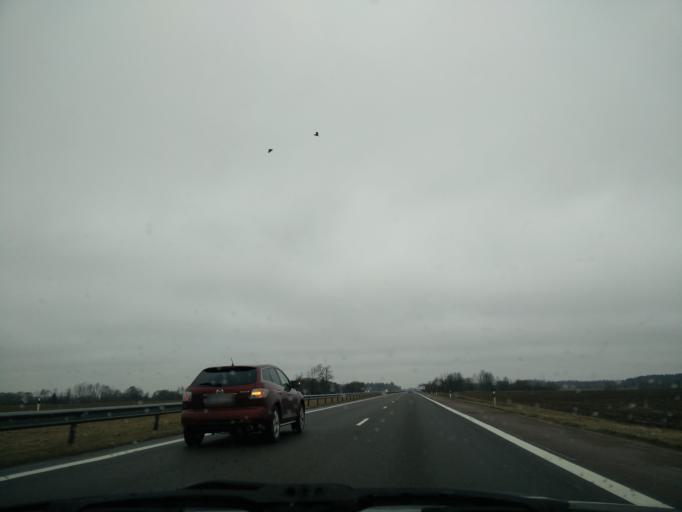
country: LT
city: Raseiniai
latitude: 55.3802
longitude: 22.9245
